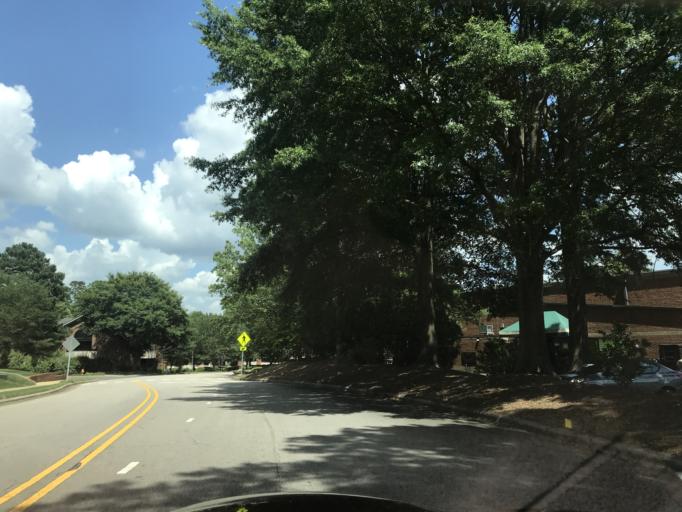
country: US
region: North Carolina
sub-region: Wake County
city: West Raleigh
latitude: 35.8264
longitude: -78.7068
